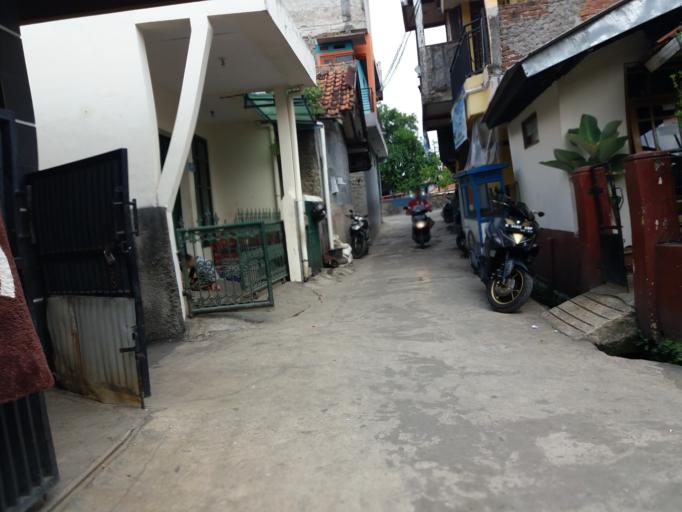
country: ID
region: West Java
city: Bandung
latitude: -6.9200
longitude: 107.6535
